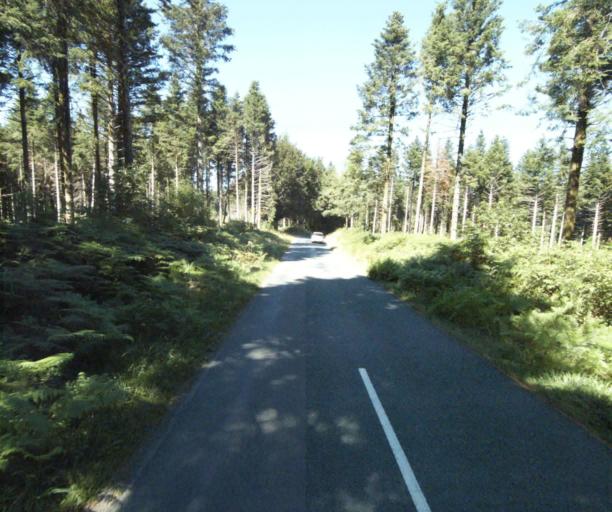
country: FR
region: Midi-Pyrenees
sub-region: Departement du Tarn
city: Dourgne
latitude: 43.4333
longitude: 2.1273
